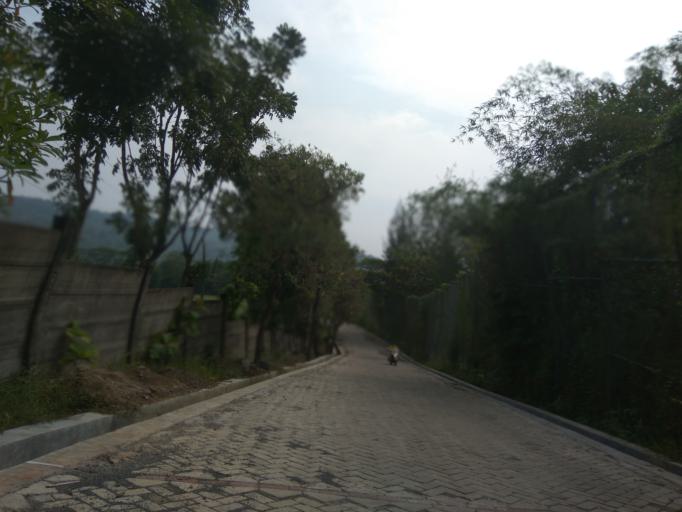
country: ID
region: Central Java
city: Semarang
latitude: -7.0354
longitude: 110.4118
